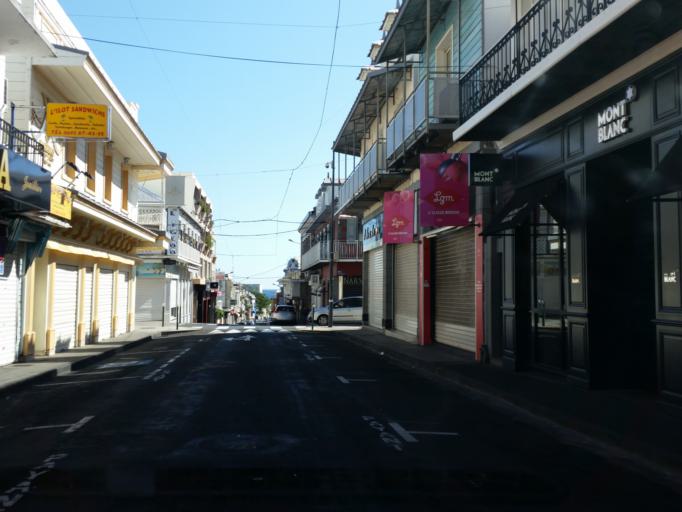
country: RE
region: Reunion
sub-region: Reunion
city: Saint-Denis
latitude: -20.8785
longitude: 55.4499
